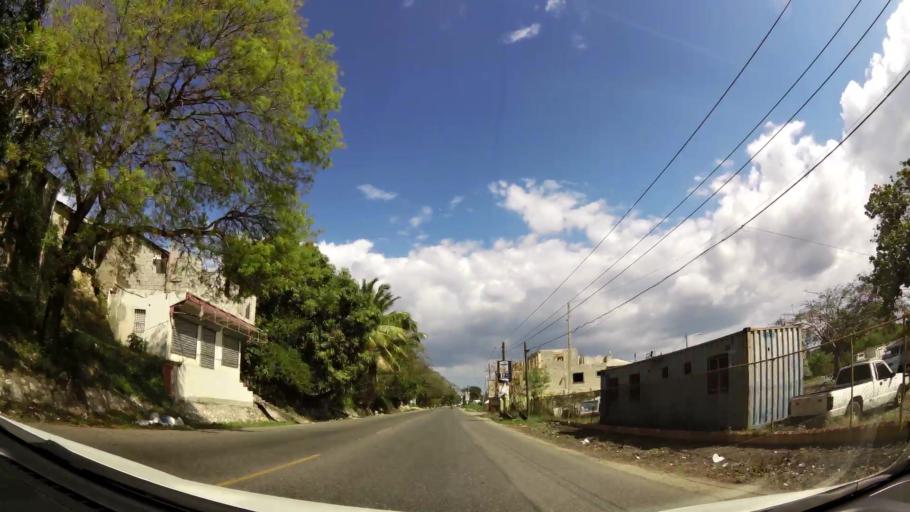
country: DO
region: San Cristobal
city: San Cristobal
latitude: 18.4271
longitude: -70.0772
